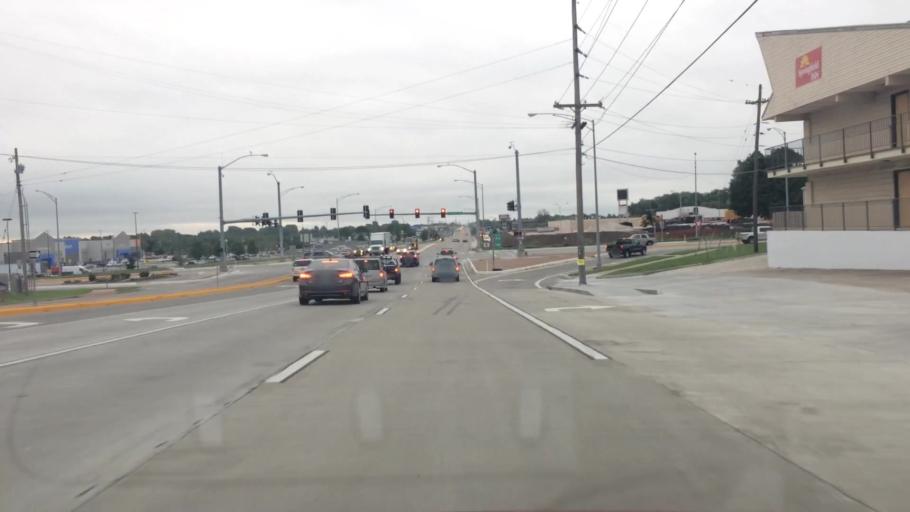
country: US
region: Missouri
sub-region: Greene County
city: Springfield
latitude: 37.2401
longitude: -93.2644
